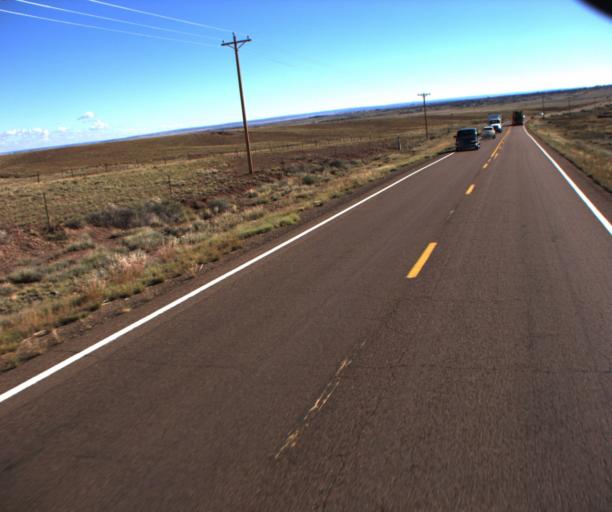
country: US
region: Arizona
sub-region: Apache County
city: Saint Johns
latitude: 34.5096
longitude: -109.4663
